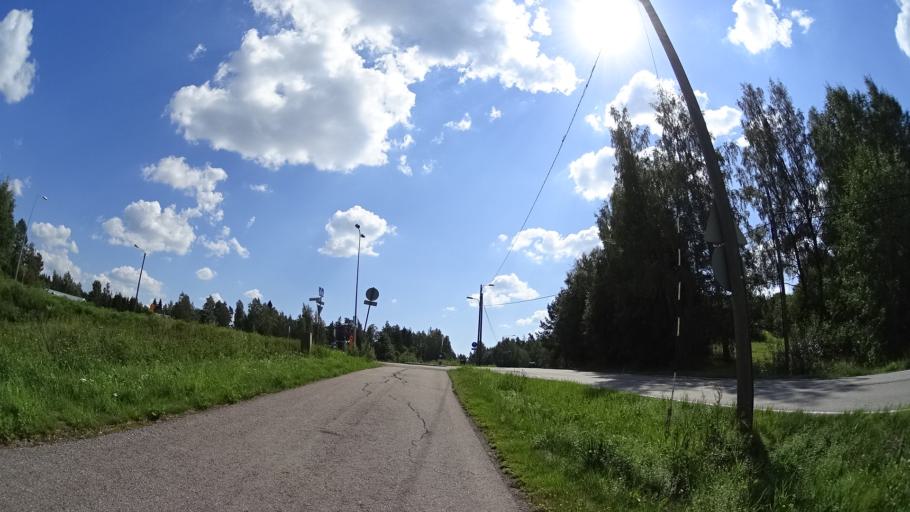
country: FI
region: Uusimaa
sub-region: Helsinki
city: Tuusula
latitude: 60.3674
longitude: 24.9781
